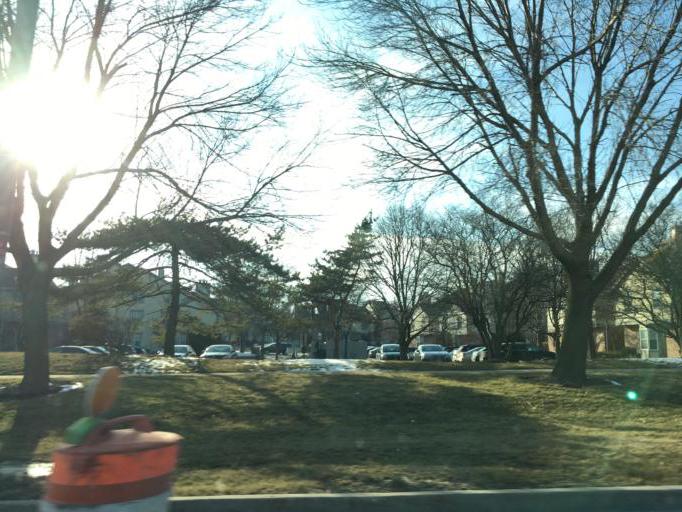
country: US
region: Illinois
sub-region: Cook County
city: Hoffman Estates
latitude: 42.0604
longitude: -88.0797
